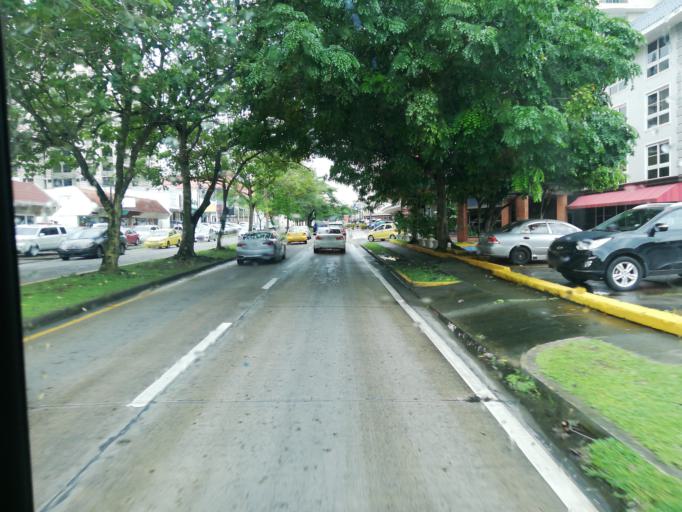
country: PA
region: Panama
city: Panama
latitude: 9.0062
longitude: -79.5396
